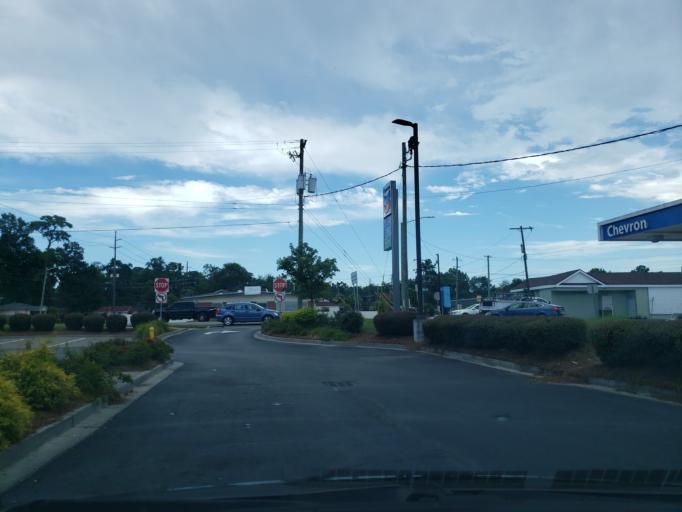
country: US
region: Georgia
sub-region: Chatham County
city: Thunderbolt
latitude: 32.0382
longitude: -81.0663
